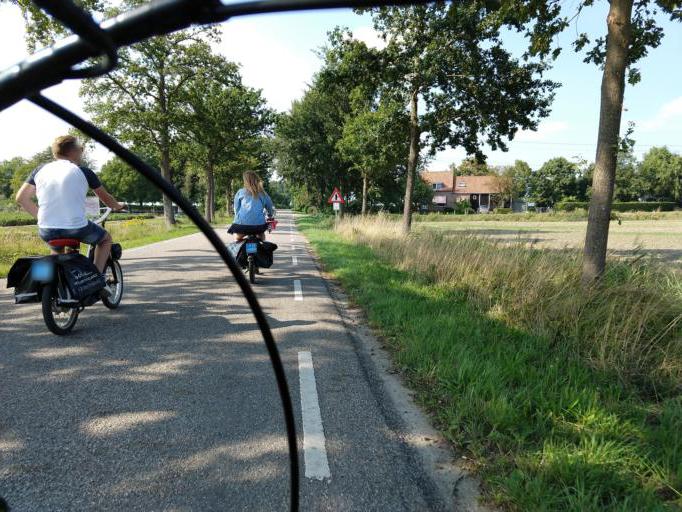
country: NL
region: Zeeland
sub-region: Gemeente Terneuzen
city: Terneuzen
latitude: 51.4137
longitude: 3.8426
